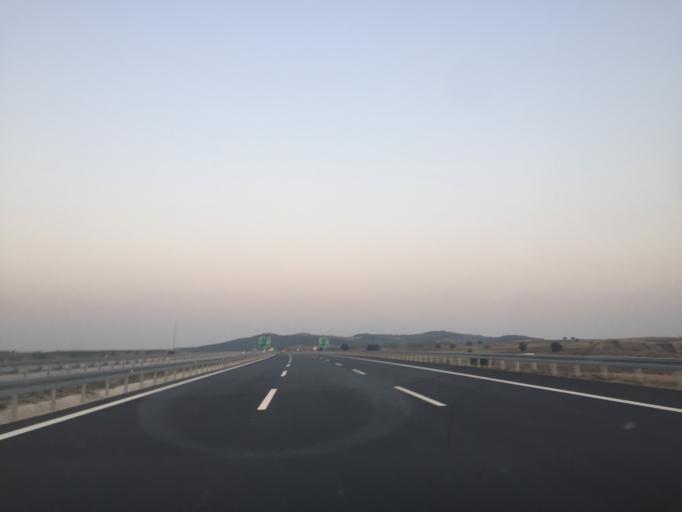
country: TR
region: Bursa
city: Mahmudiye
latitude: 40.2581
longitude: 28.6892
